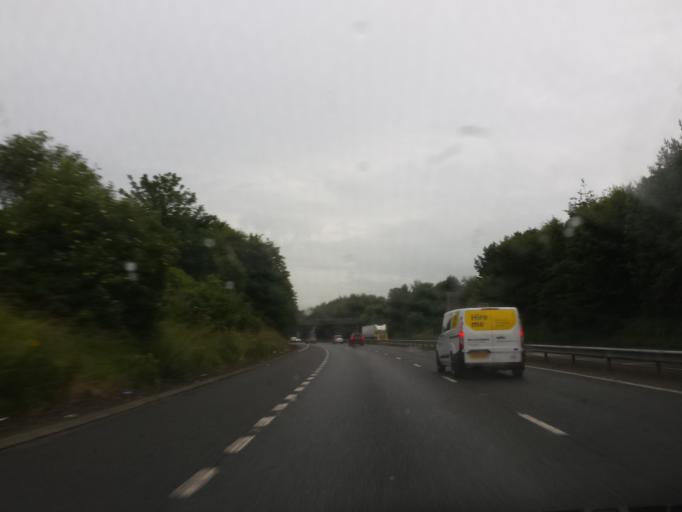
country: GB
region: Scotland
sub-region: Perth and Kinross
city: Perth
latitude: 56.3863
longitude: -3.4829
